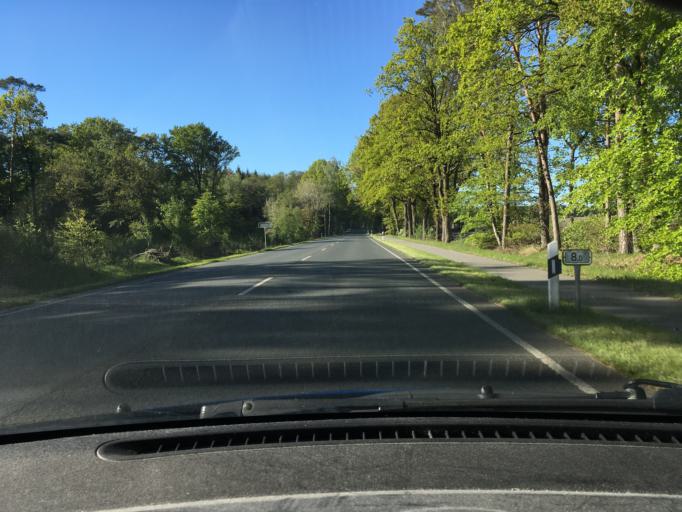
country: DE
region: Lower Saxony
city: Soltau
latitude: 53.0569
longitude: 9.8581
